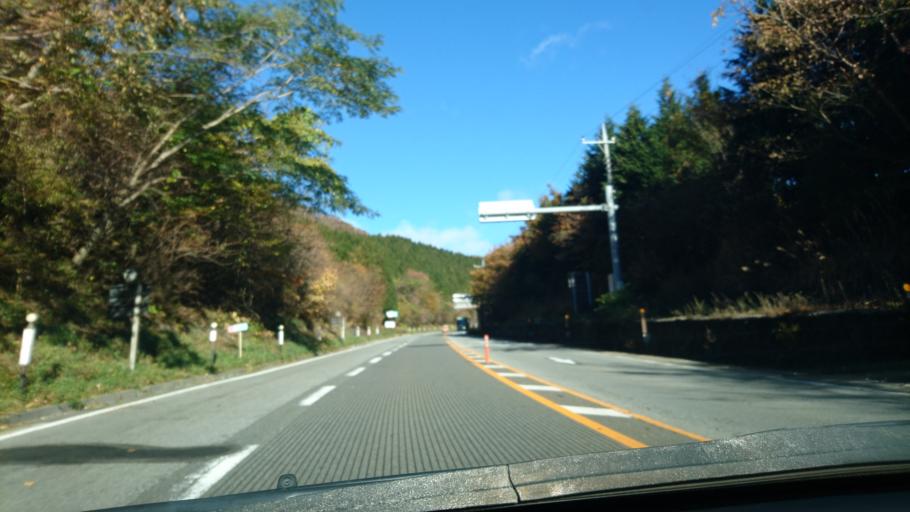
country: JP
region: Nagano
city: Saku
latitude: 36.3141
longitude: 138.6510
